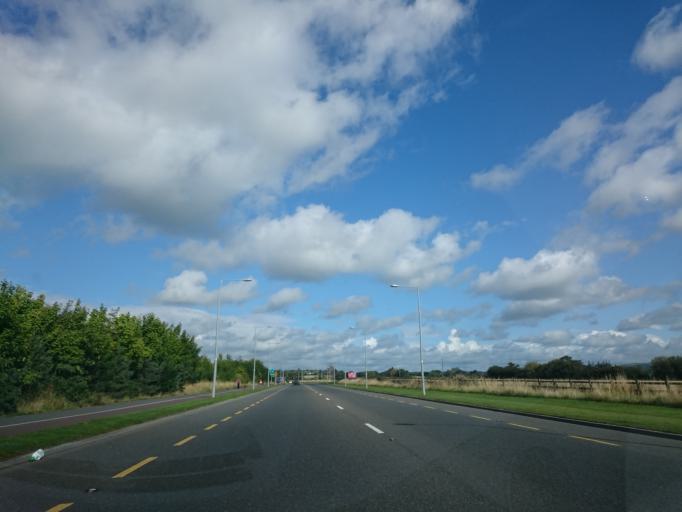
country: IE
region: Leinster
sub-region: Kilkenny
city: Kilkenny
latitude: 52.6666
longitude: -7.2287
